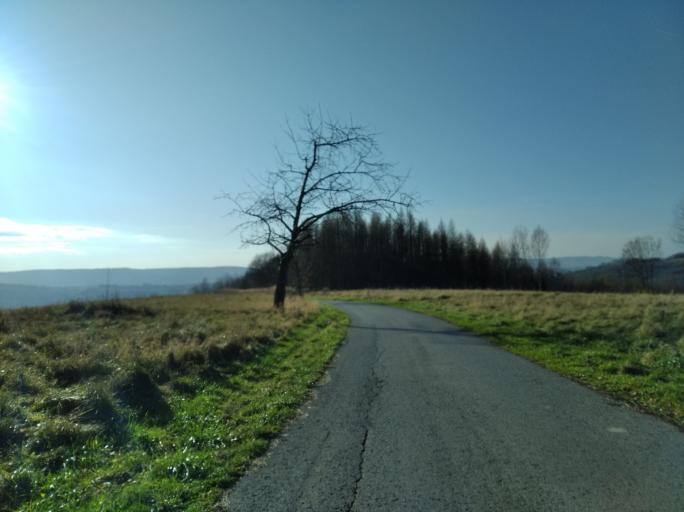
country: PL
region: Subcarpathian Voivodeship
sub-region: Powiat strzyzowski
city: Strzyzow
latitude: 49.8809
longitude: 21.8321
